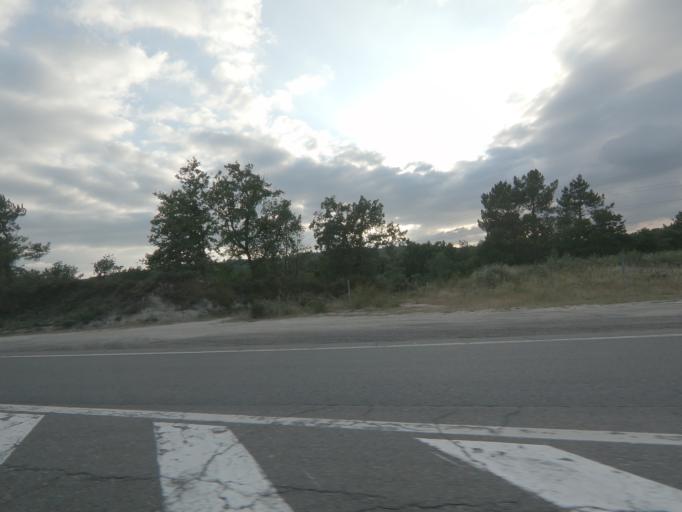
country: ES
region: Galicia
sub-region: Provincia de Ourense
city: Taboadela
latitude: 42.2581
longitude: -7.8325
